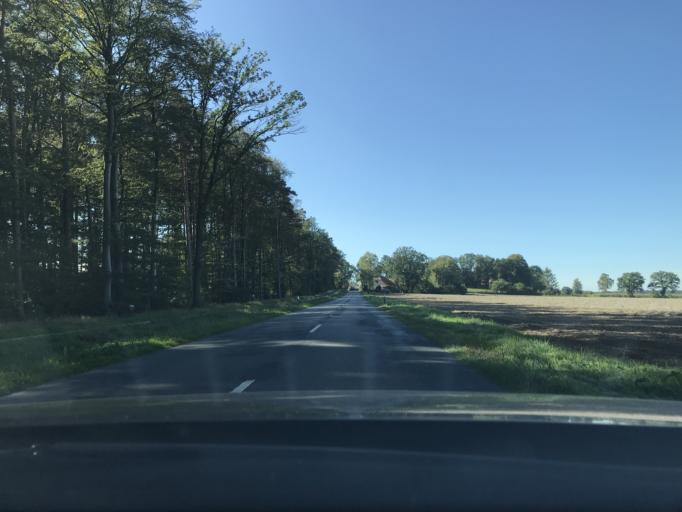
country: DE
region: Lower Saxony
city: Gerdau
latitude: 52.9556
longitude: 10.4042
